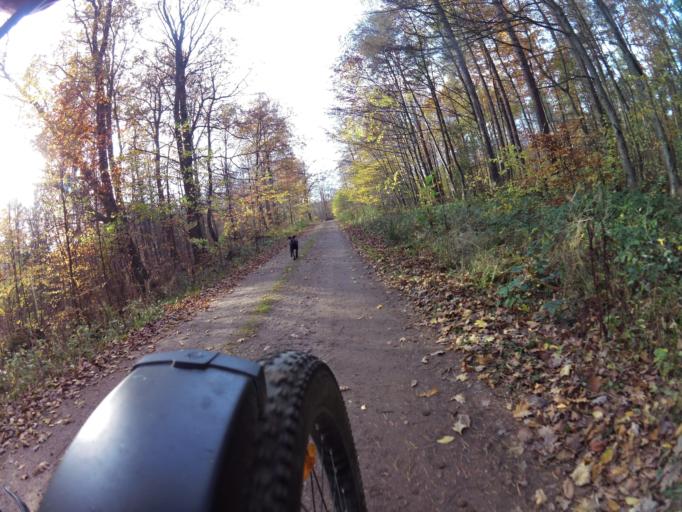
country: PL
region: Pomeranian Voivodeship
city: Strzelno
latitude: 54.7414
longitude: 18.2810
